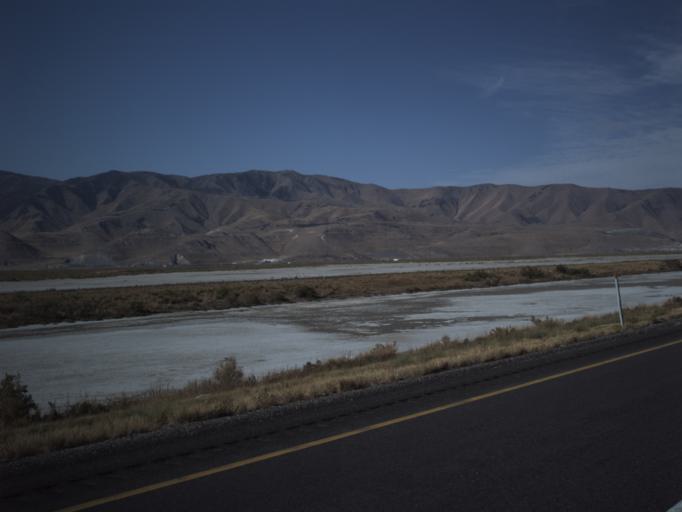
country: US
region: Utah
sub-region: Tooele County
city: Grantsville
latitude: 40.7039
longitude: -112.5039
